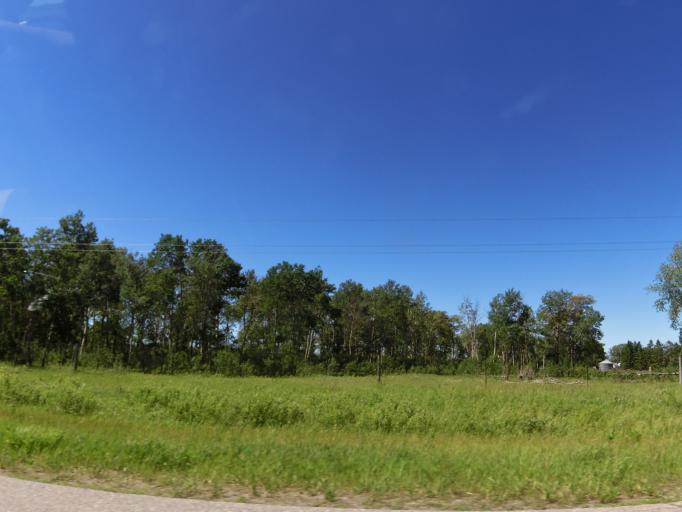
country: US
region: Minnesota
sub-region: Red Lake County
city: Red Lake Falls
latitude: 47.7170
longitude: -96.1771
